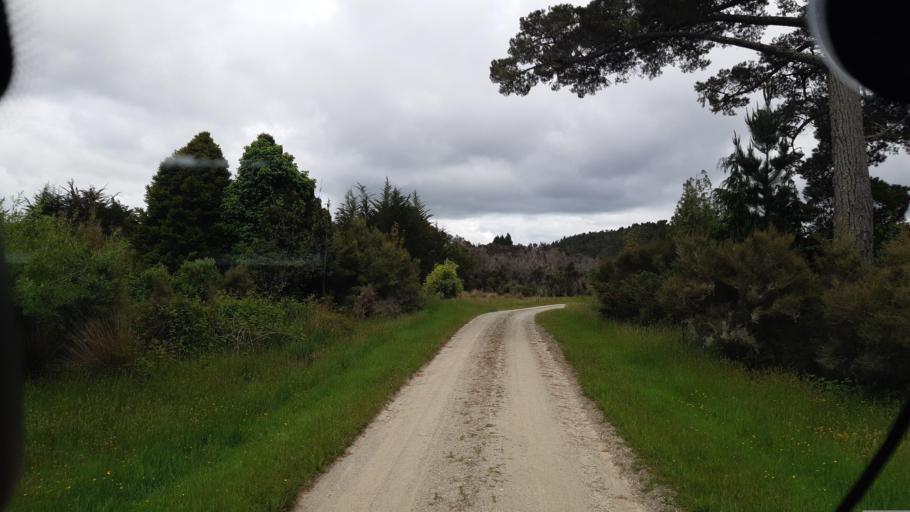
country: NZ
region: West Coast
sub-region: Buller District
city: Westport
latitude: -42.2953
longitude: 171.8220
